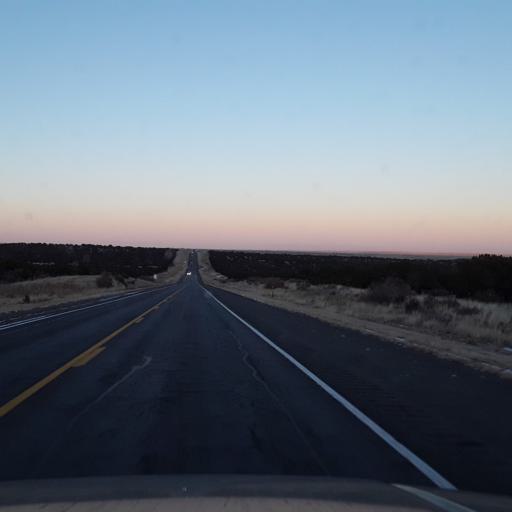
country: US
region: New Mexico
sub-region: Torrance County
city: Estancia
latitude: 34.5228
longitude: -105.3299
